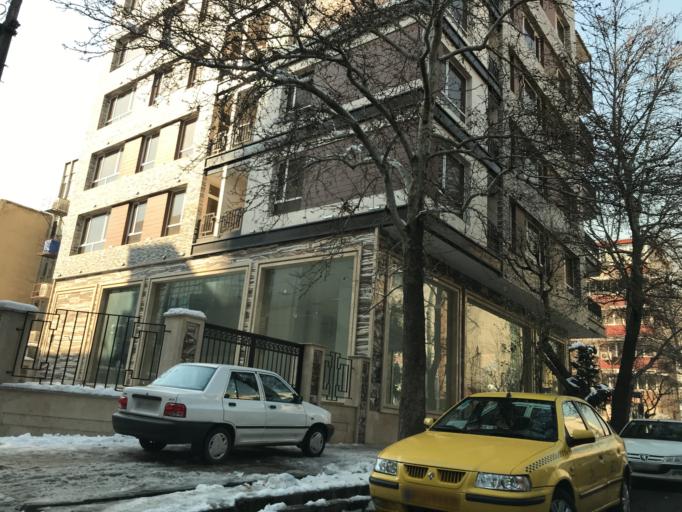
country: IR
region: Tehran
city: Tehran
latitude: 35.7106
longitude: 51.3982
